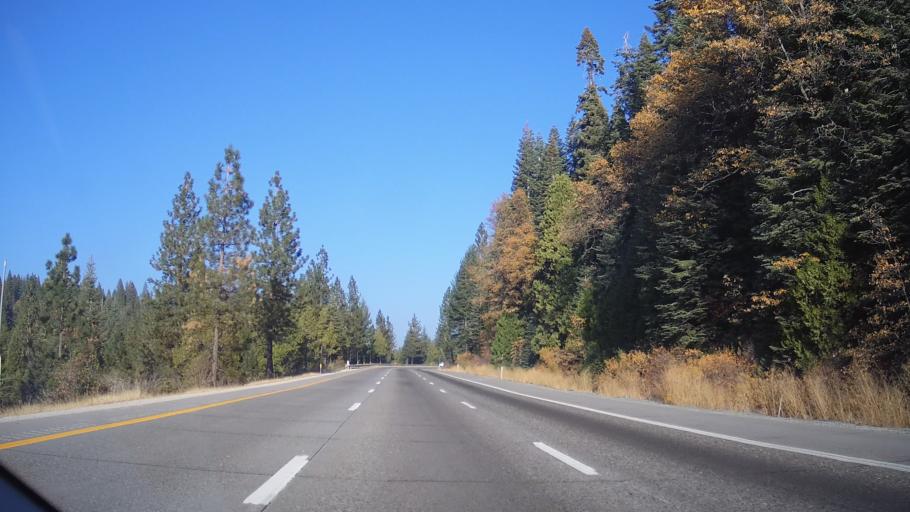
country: US
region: California
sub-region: Placer County
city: Foresthill
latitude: 39.2513
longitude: -120.7391
